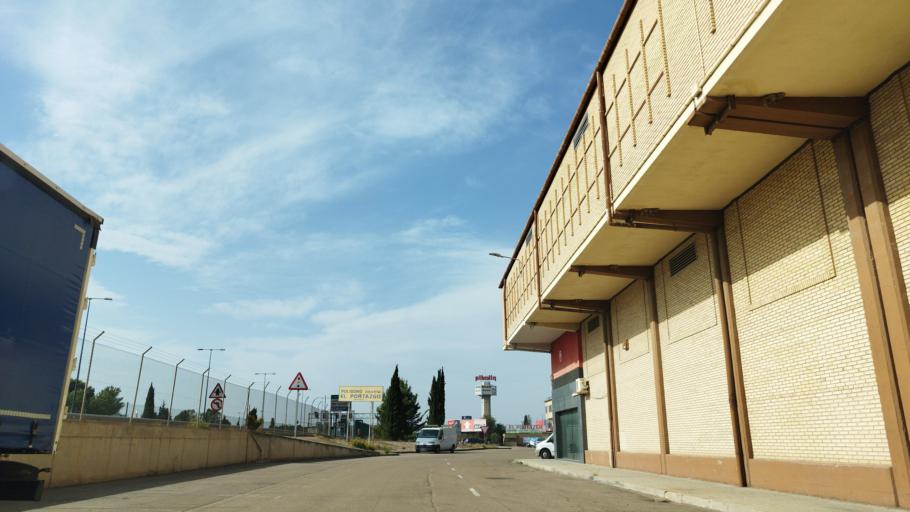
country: ES
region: Aragon
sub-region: Provincia de Zaragoza
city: Oliver-Valdefierro, Oliver, Valdefierro
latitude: 41.6721
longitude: -0.9481
